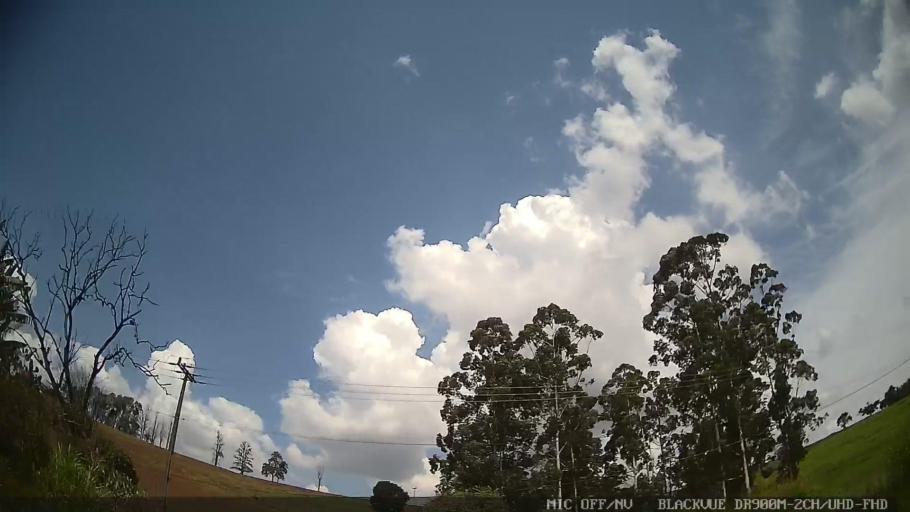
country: BR
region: Sao Paulo
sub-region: Braganca Paulista
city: Braganca Paulista
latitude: -22.9478
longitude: -46.6884
